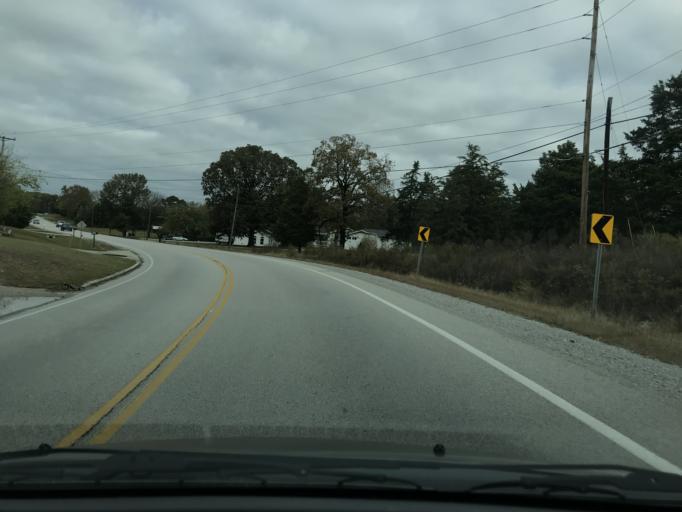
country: US
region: Tennessee
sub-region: Hamilton County
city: Collegedale
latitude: 35.1342
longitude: -85.0430
